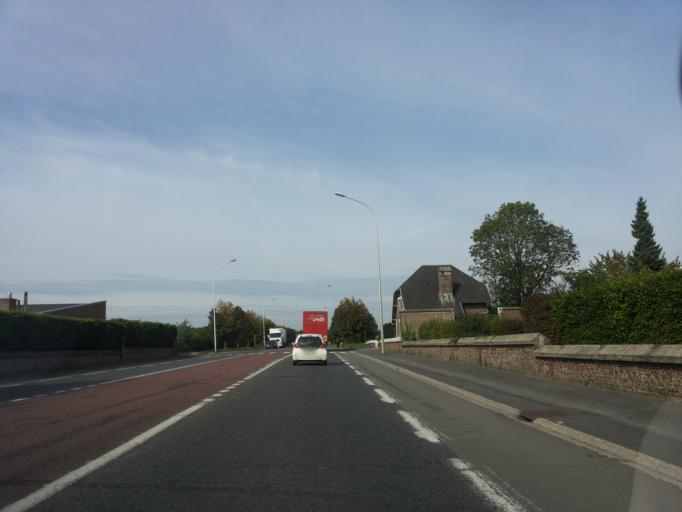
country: FR
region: Nord-Pas-de-Calais
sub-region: Departement du Pas-de-Calais
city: Tilloy-les-Mofflaines
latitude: 50.2810
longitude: 2.8110
